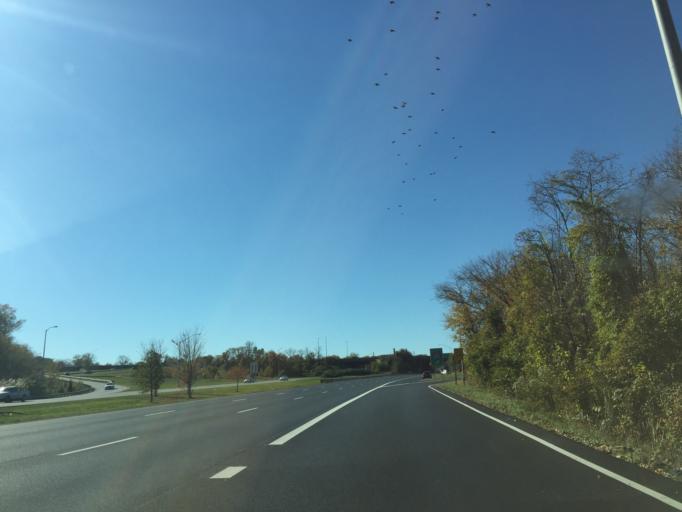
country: US
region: Maryland
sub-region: Anne Arundel County
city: Linthicum
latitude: 39.2212
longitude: -76.6554
